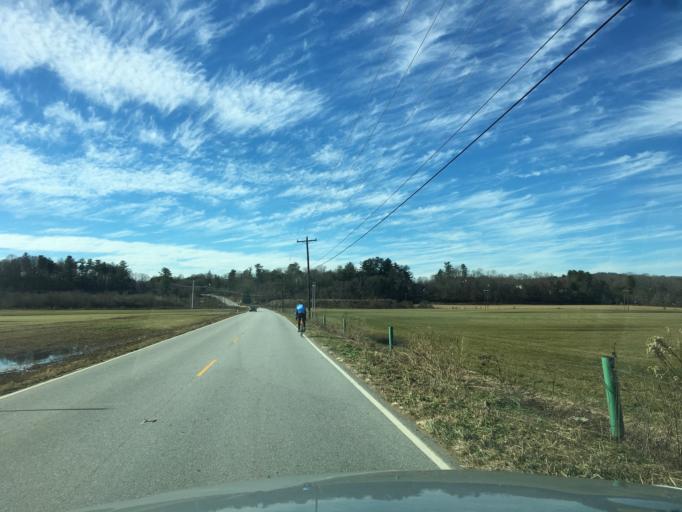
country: US
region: North Carolina
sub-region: Henderson County
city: Mills River
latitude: 35.4070
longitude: -82.5335
